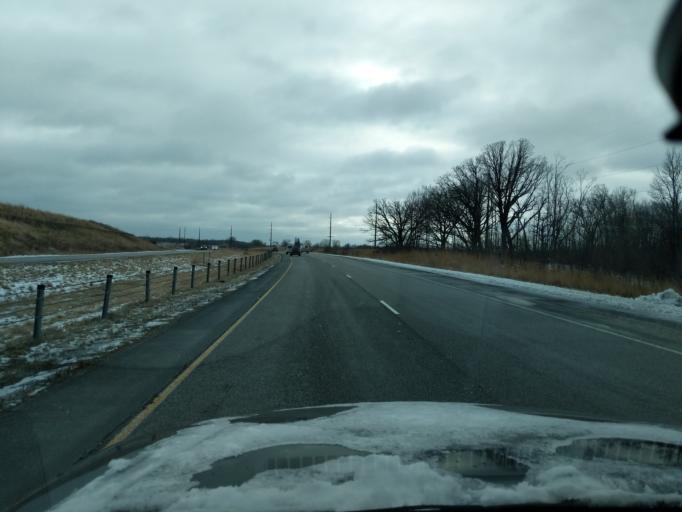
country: US
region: Minnesota
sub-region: Carver County
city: Chaska
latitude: 44.7996
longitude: -93.6304
